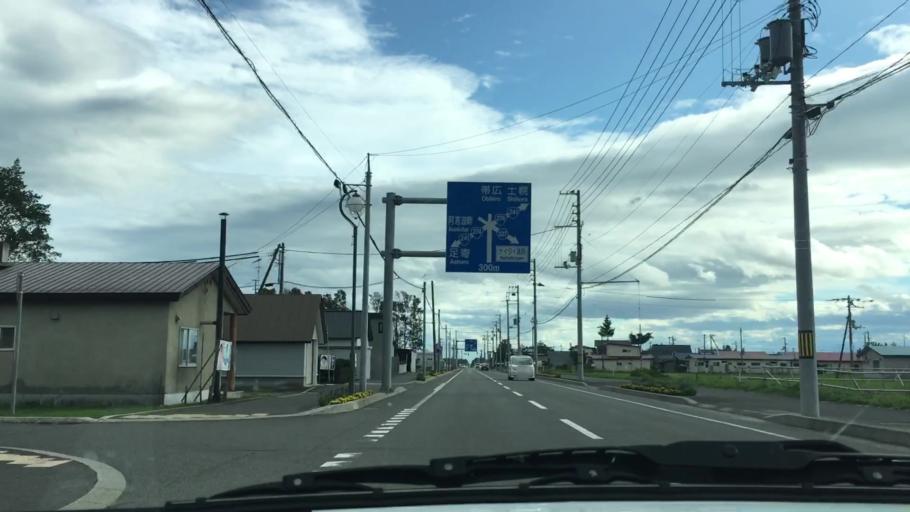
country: JP
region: Hokkaido
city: Otofuke
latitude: 43.2282
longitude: 143.2941
